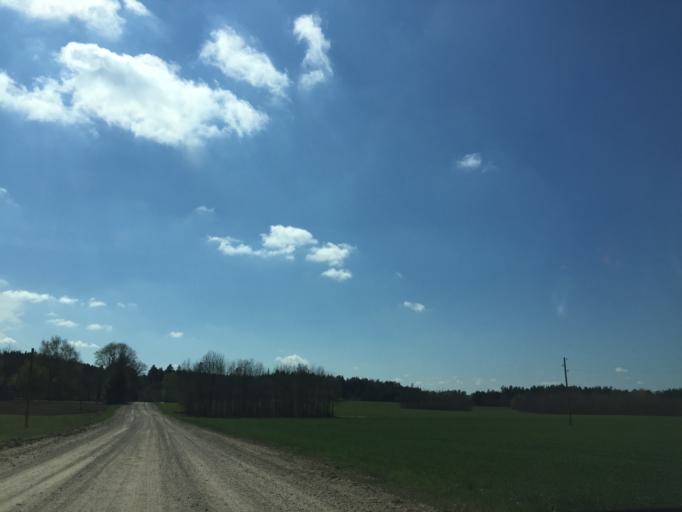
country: LV
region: Smiltene
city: Smiltene
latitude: 57.5844
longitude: 25.9440
